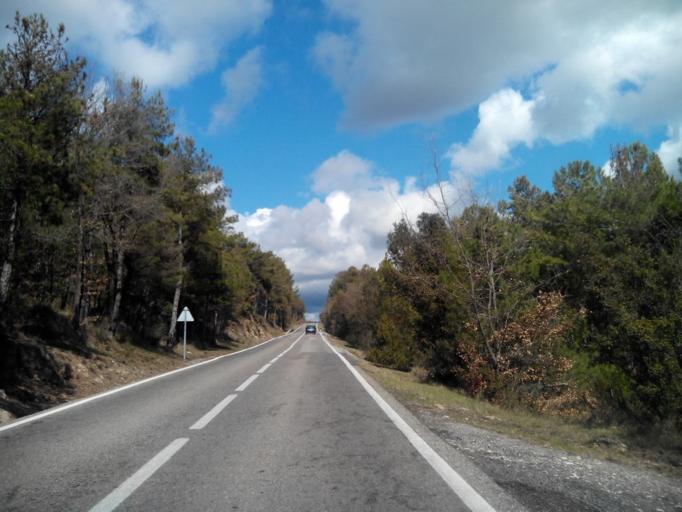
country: ES
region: Catalonia
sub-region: Provincia de Barcelona
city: Cardona
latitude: 41.9437
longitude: 1.6984
